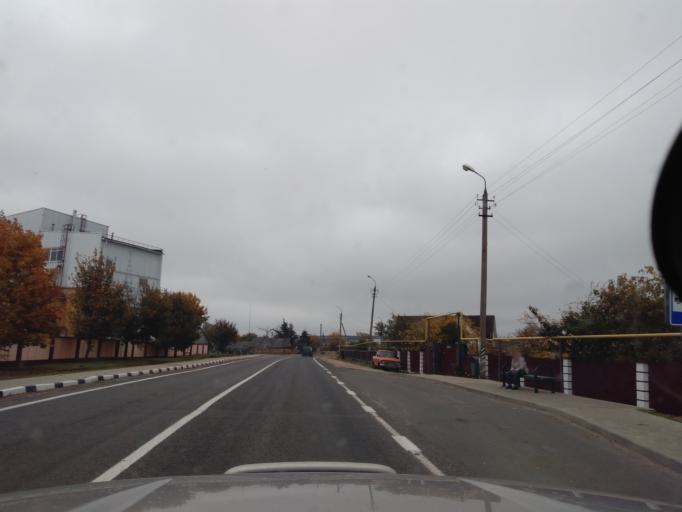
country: BY
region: Minsk
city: Kapyl'
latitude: 53.1420
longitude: 27.0905
